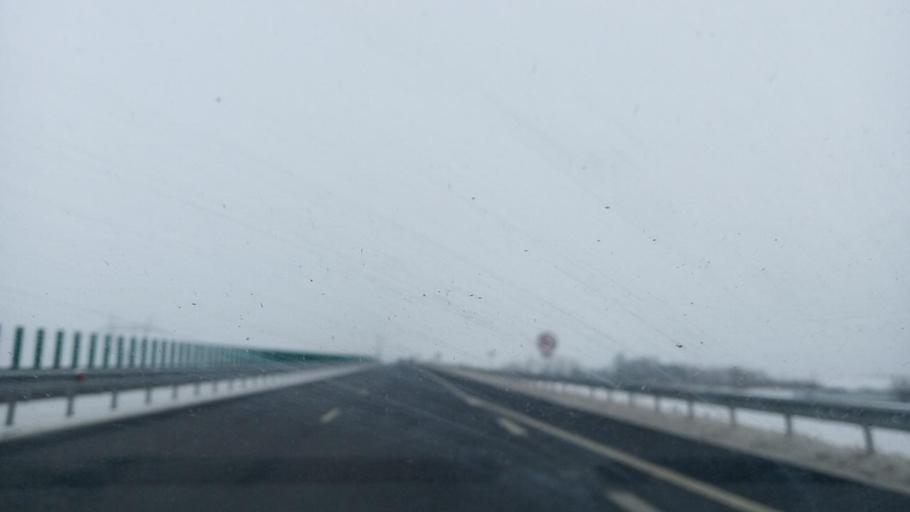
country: RO
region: Bacau
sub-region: Comuna Letea Veche
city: Holt
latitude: 46.5978
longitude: 26.9606
